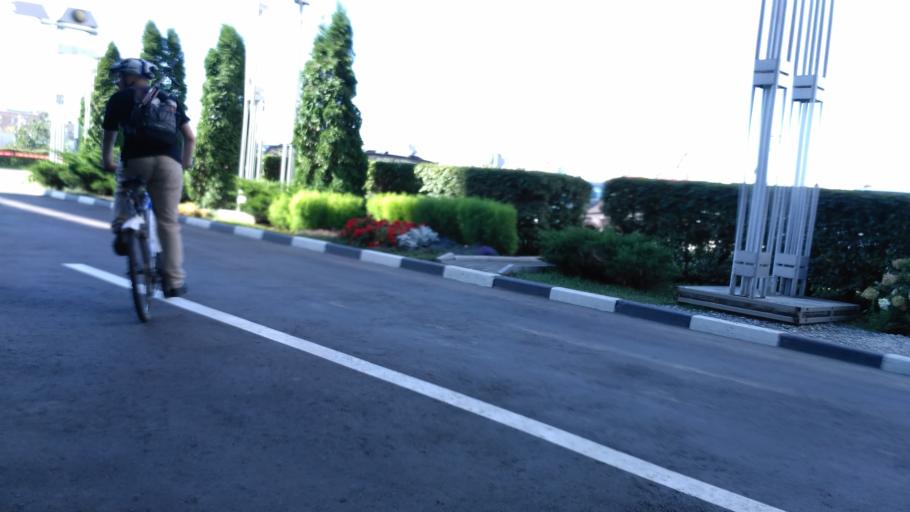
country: RU
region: Moskovskaya
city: Bogorodskoye
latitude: 55.7908
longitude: 37.7474
